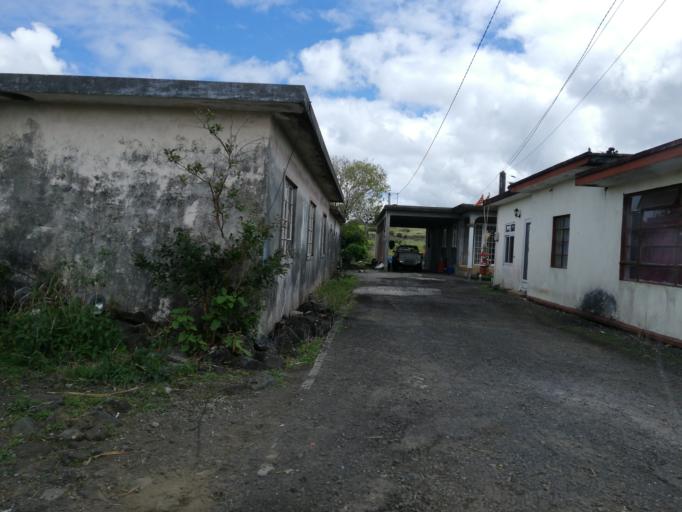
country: MU
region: Moka
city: Quartier Militaire
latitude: -20.2259
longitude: 57.5951
